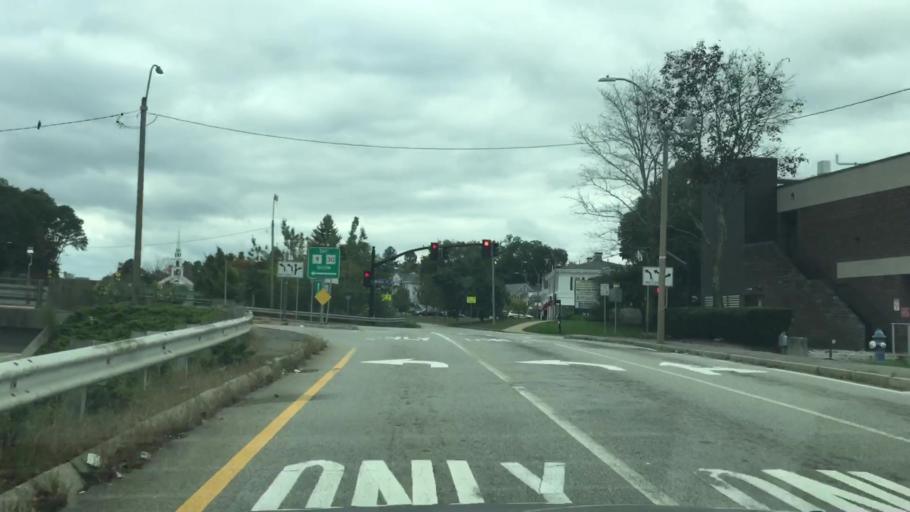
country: US
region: Massachusetts
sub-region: Middlesex County
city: Framingham Center
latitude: 42.3002
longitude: -71.4332
